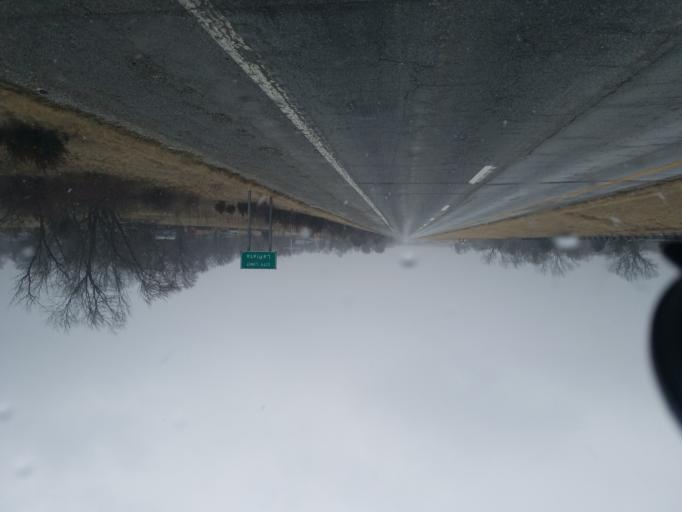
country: US
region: Missouri
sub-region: Macon County
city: La Plata
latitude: 40.0305
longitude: -92.4856
